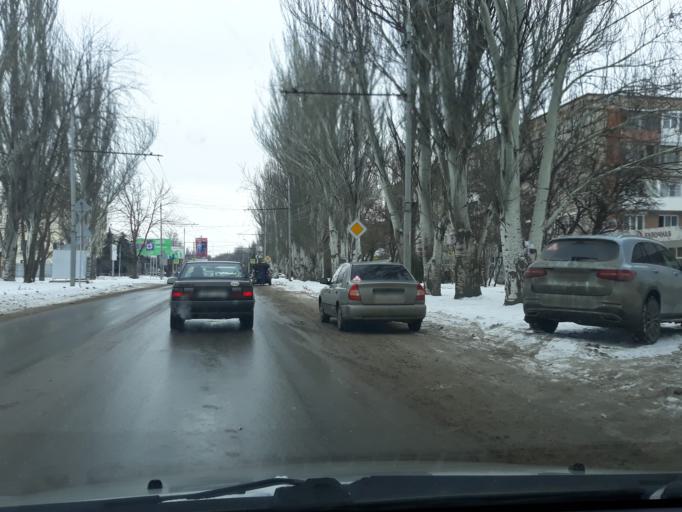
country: RU
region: Rostov
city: Taganrog
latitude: 47.2479
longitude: 38.9178
